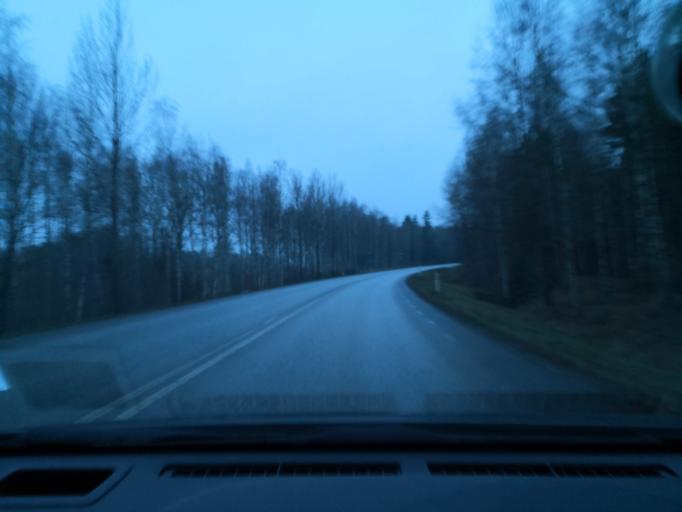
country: SE
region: Soedermanland
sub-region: Eskilstuna Kommun
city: Skogstorp
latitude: 59.3285
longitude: 16.4640
